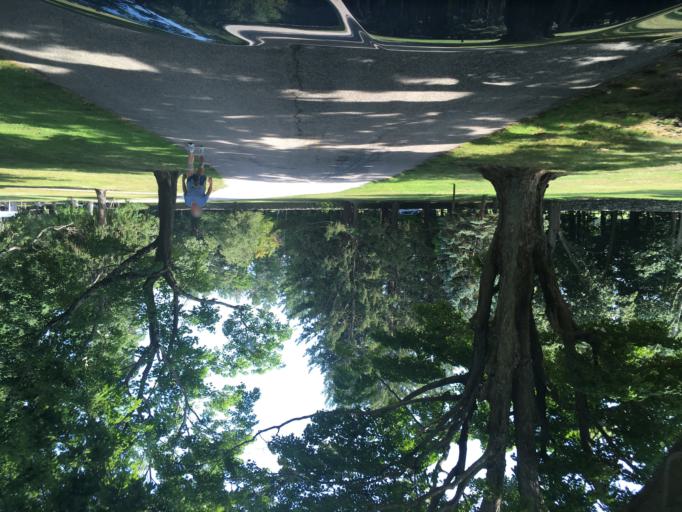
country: US
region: Rhode Island
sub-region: Kent County
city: East Greenwich
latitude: 41.6537
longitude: -71.4392
